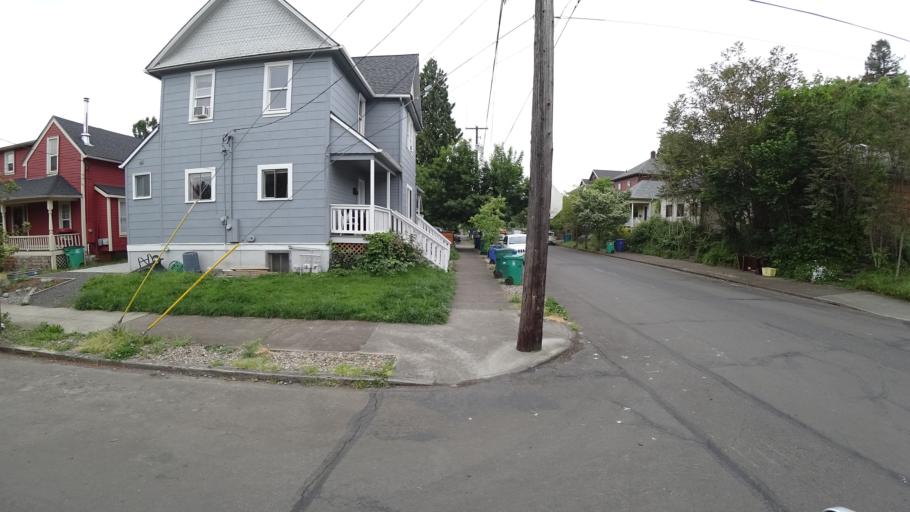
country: US
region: Oregon
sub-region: Multnomah County
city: Portland
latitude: 45.5545
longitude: -122.6595
